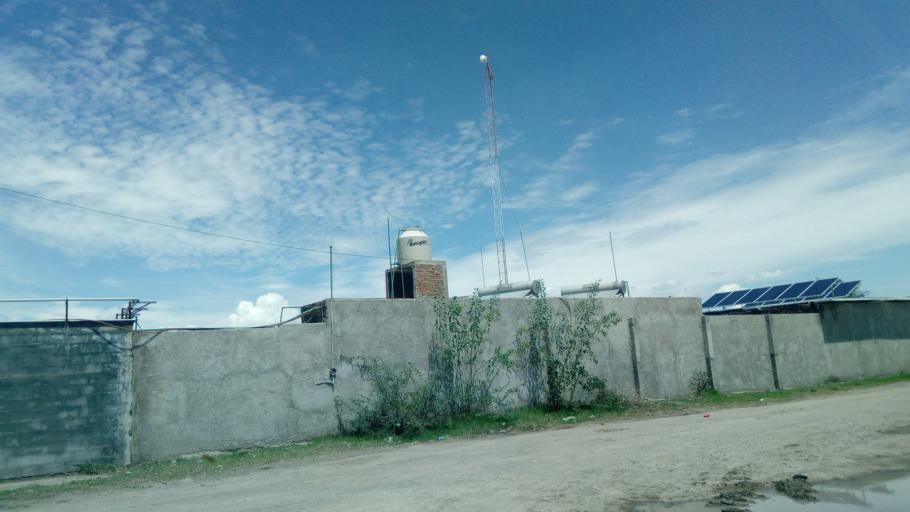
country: MX
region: Durango
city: Victoria de Durango
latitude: 24.0137
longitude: -104.5907
